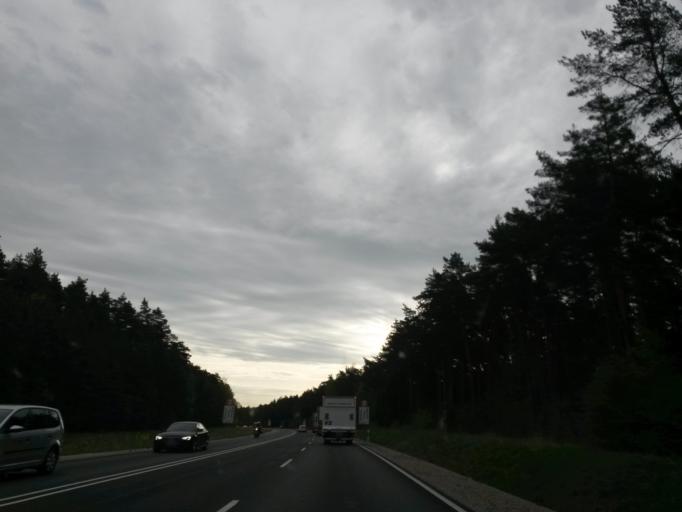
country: DE
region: Bavaria
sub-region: Upper Franconia
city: Pommersfelden
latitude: 49.7545
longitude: 10.8556
